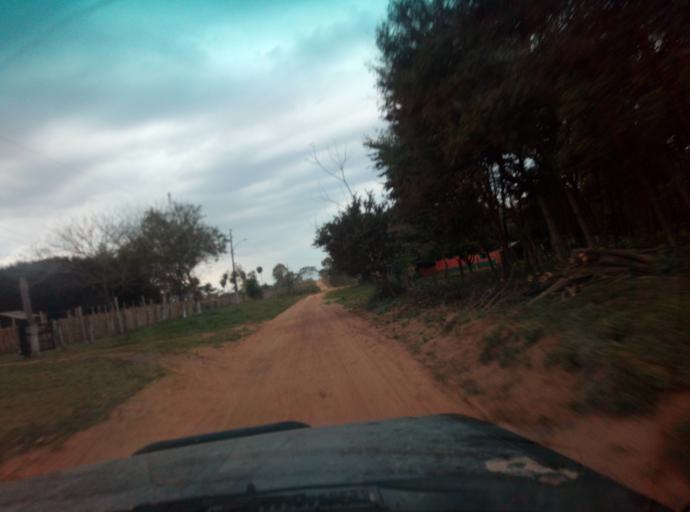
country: PY
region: Caaguazu
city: Doctor Cecilio Baez
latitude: -25.1403
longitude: -56.2238
